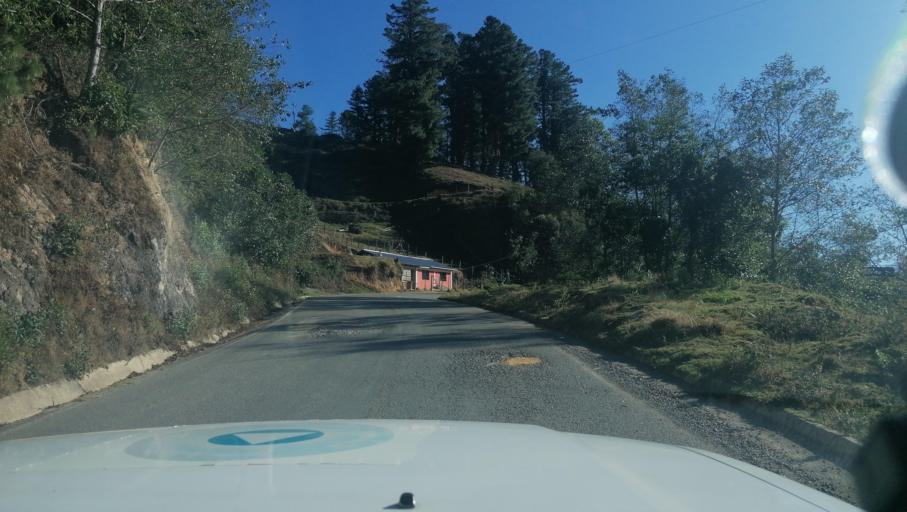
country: MX
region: Chiapas
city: Motozintla de Mendoza
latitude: 15.2374
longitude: -92.2351
